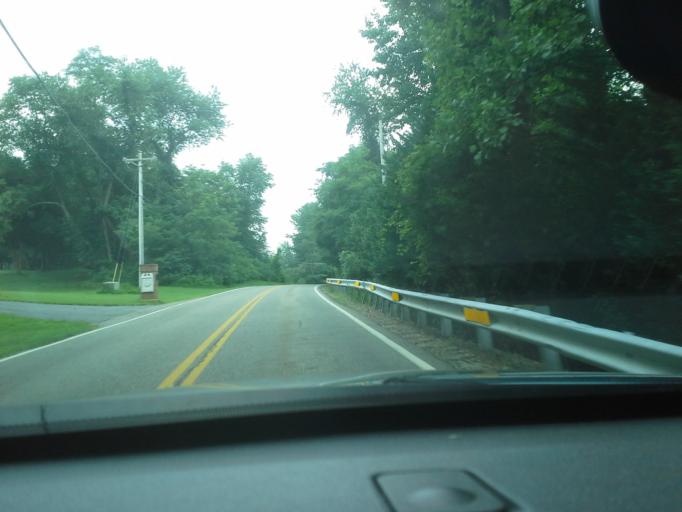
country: US
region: Maryland
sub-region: Calvert County
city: Dunkirk Town Center
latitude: 38.7315
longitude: -76.6422
